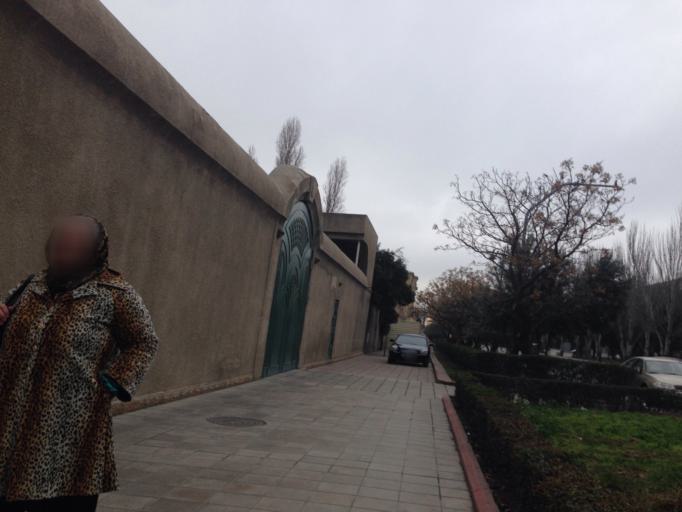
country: AZ
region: Baki
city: Bilajari
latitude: 40.4111
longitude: 49.8479
